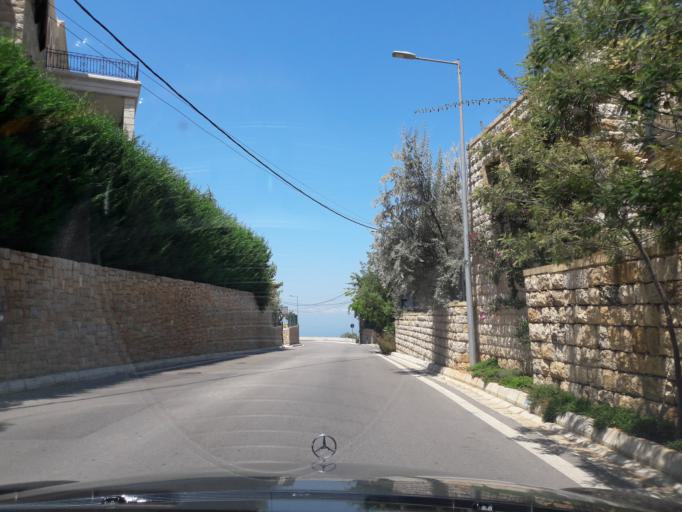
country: LB
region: Mont-Liban
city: Djounie
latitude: 33.9202
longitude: 35.6380
